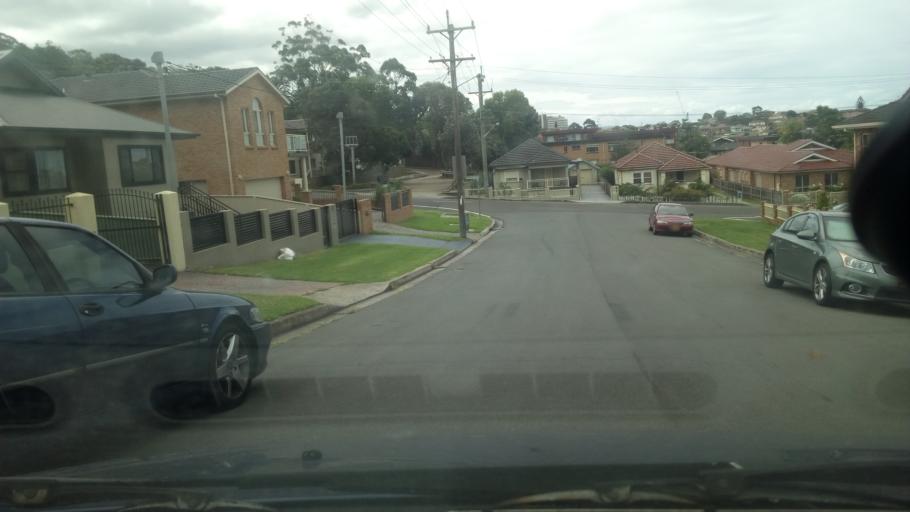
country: AU
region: New South Wales
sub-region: Wollongong
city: Mangerton
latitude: -34.4364
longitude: 150.8813
